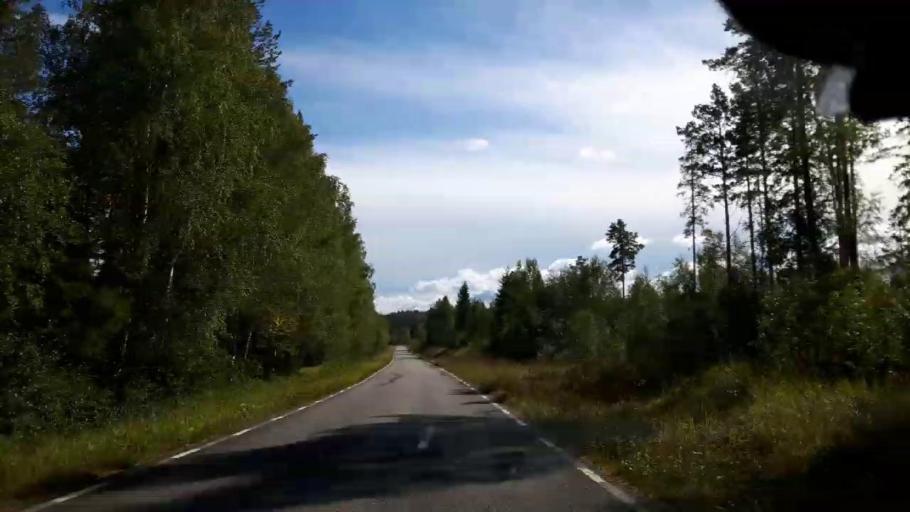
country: SE
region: Jaemtland
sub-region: OEstersunds Kommun
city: Lit
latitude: 63.2294
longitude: 15.2677
